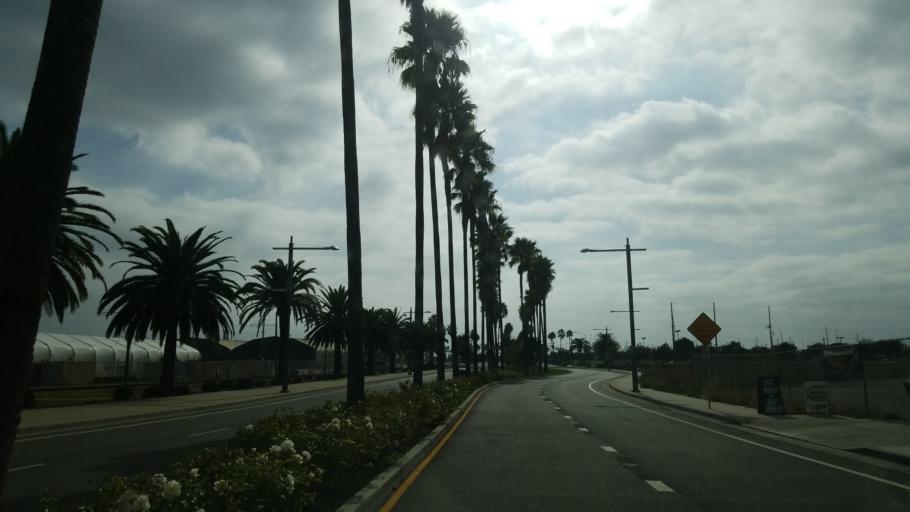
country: US
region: California
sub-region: Los Angeles County
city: San Pedro
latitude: 33.7281
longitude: -118.2789
